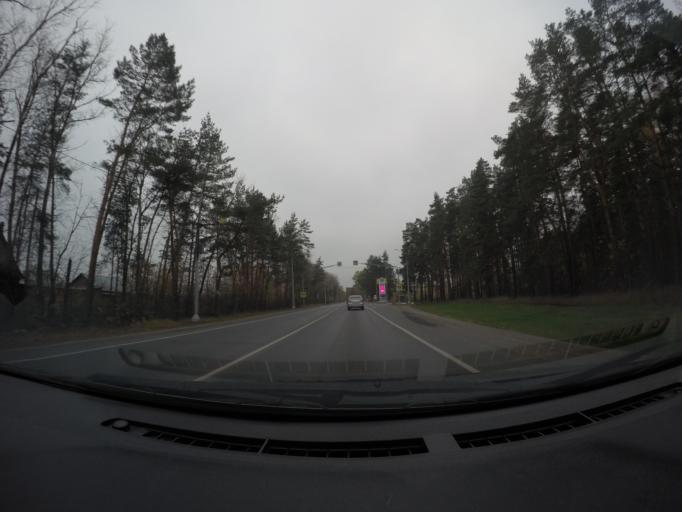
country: RU
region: Moskovskaya
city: Malyshevo
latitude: 55.4735
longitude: 38.3428
